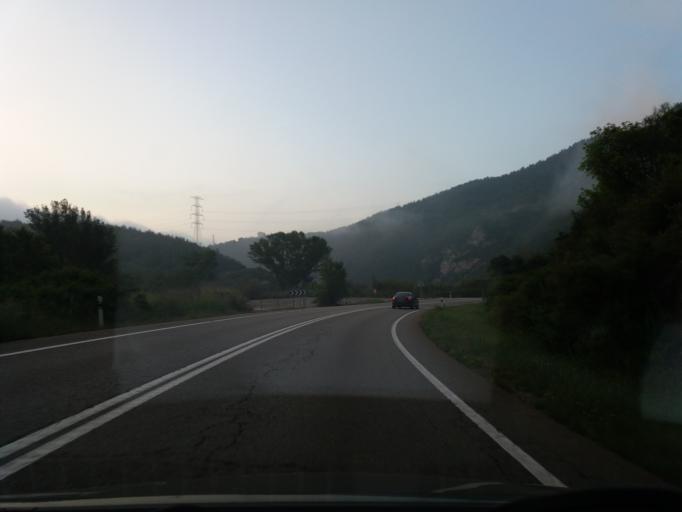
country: ES
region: Catalonia
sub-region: Provincia de Barcelona
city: Collbato
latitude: 41.5729
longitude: 1.8630
